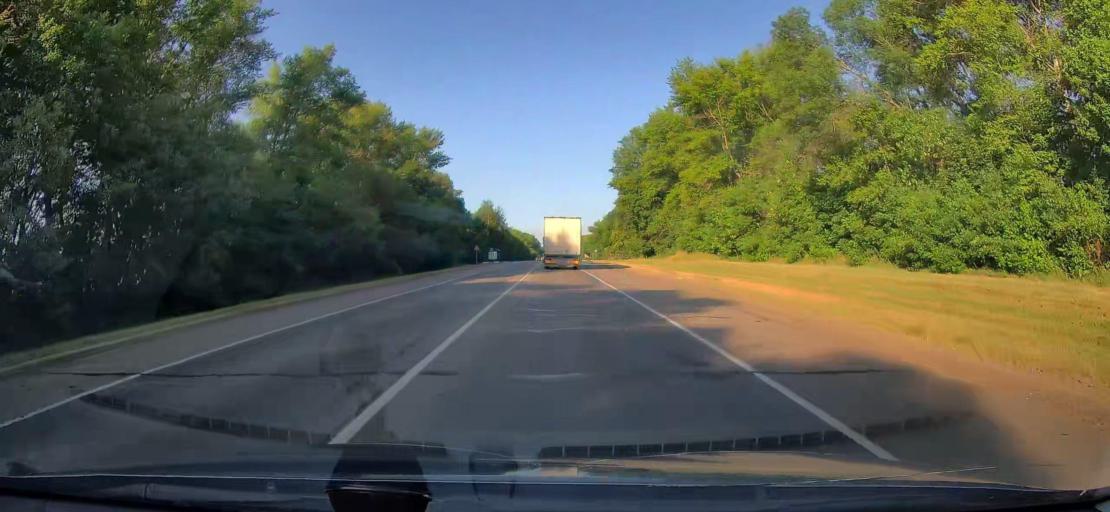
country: RU
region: Tula
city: Chern'
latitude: 53.4673
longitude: 36.9571
